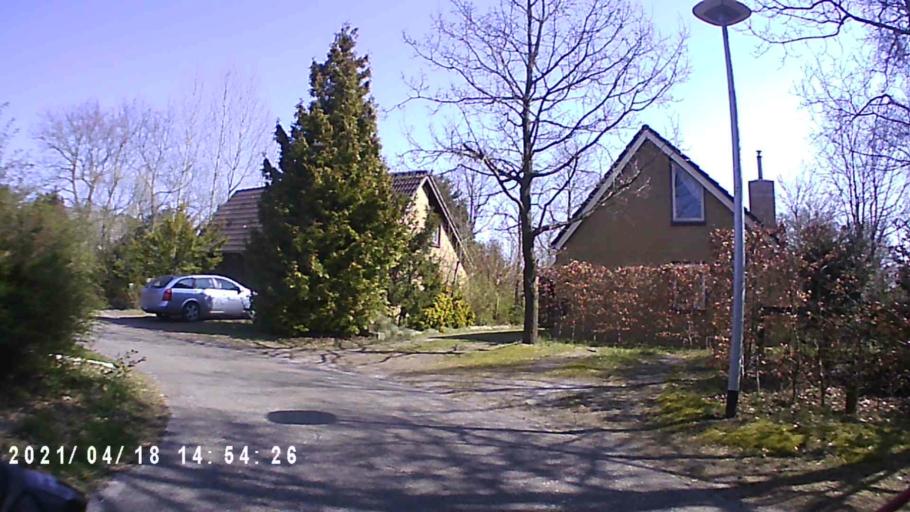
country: NL
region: Friesland
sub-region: Gemeente Dongeradeel
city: Anjum
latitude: 53.4047
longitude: 6.2183
